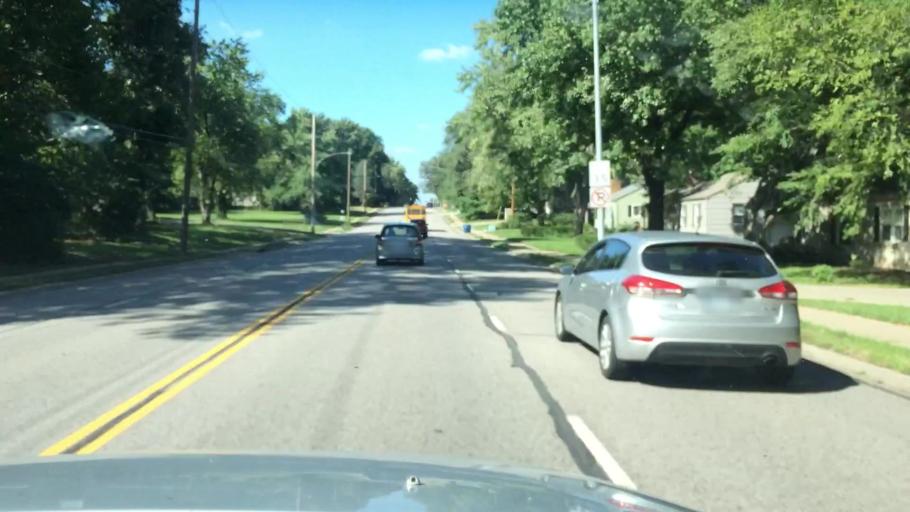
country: US
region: Kansas
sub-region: Johnson County
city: Prairie Village
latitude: 39.0041
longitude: -94.6490
